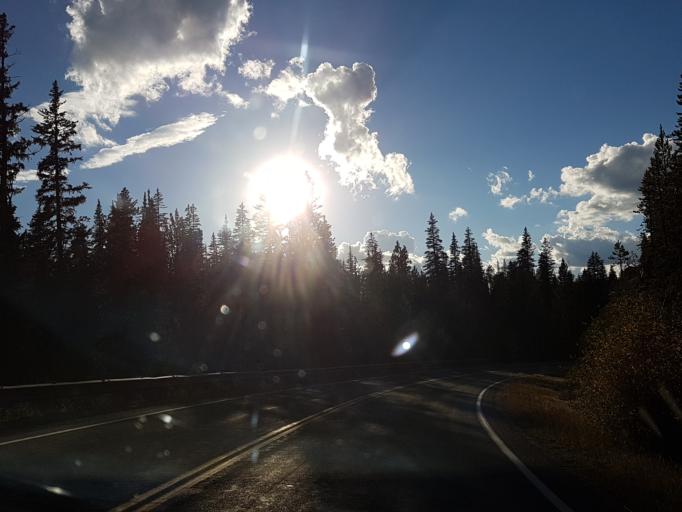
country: US
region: Montana
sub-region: Gallatin County
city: West Yellowstone
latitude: 44.4369
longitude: -110.7264
